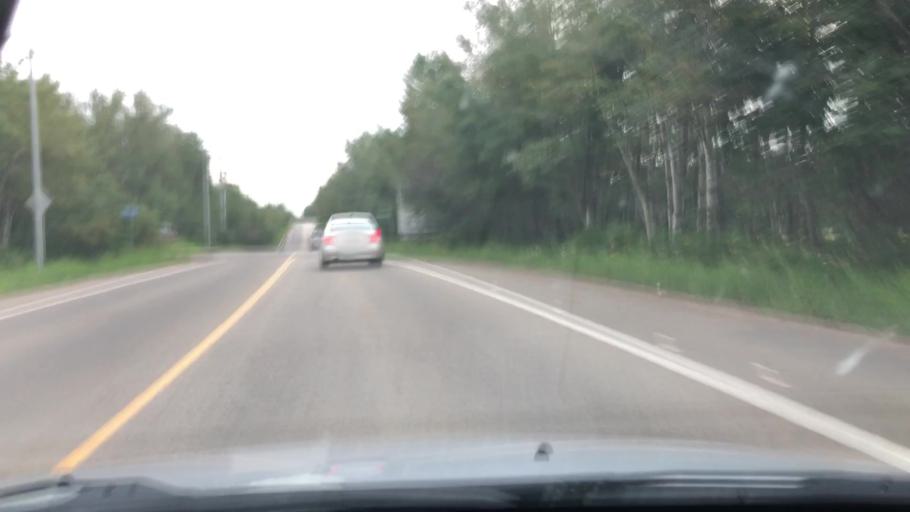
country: CA
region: Alberta
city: Devon
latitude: 53.4581
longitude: -113.6398
